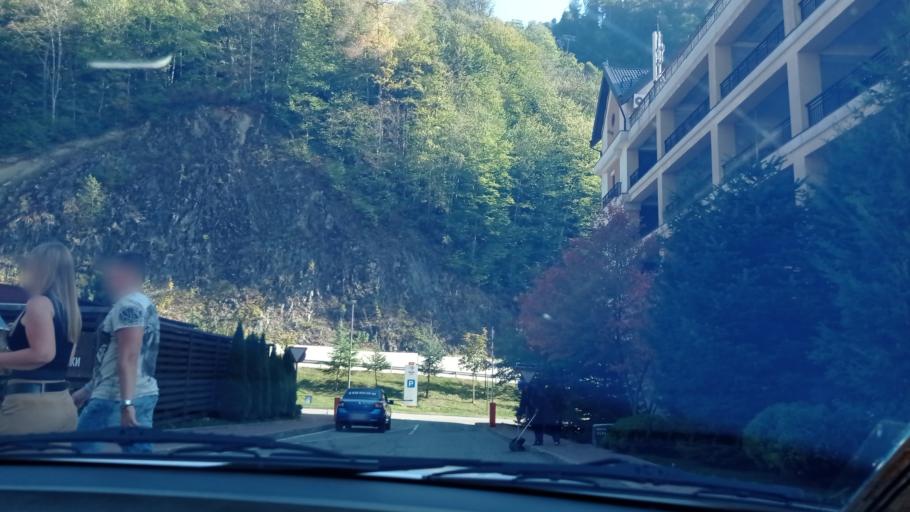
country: RU
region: Krasnodarskiy
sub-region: Sochi City
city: Krasnaya Polyana
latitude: 43.6728
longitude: 40.2987
